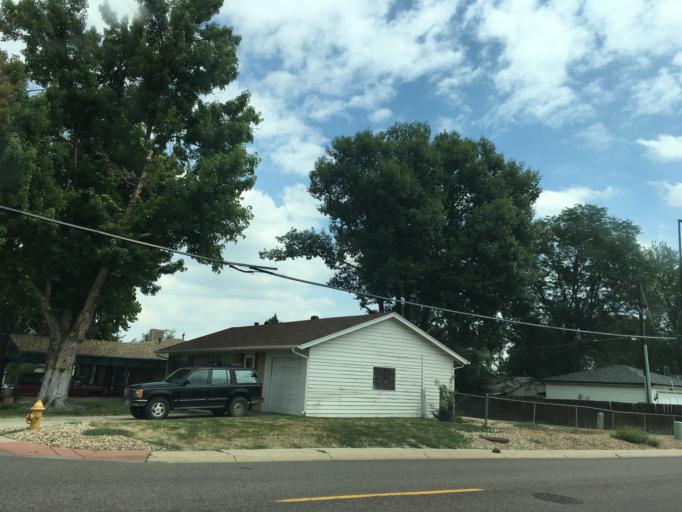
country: US
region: Colorado
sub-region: Arapahoe County
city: Sheridan
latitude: 39.6677
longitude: -105.0359
